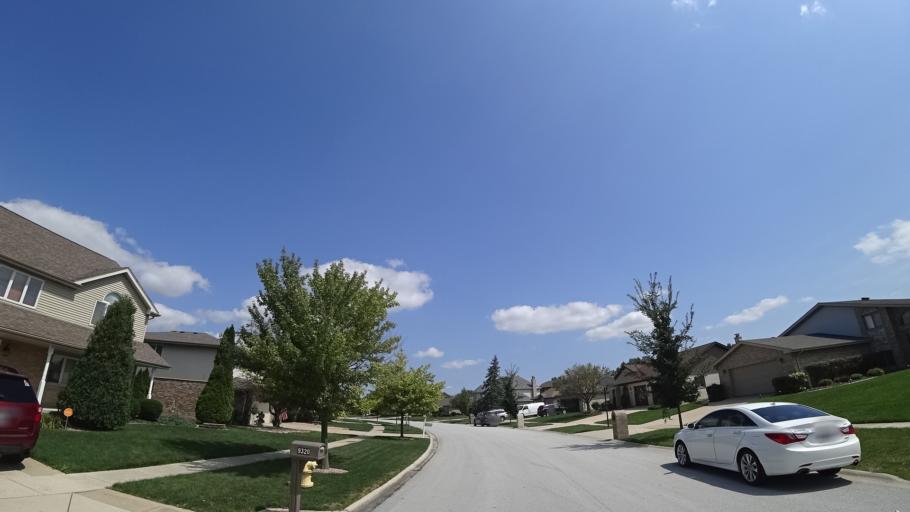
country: US
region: Illinois
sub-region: Cook County
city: Orland Hills
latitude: 41.5664
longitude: -87.8453
